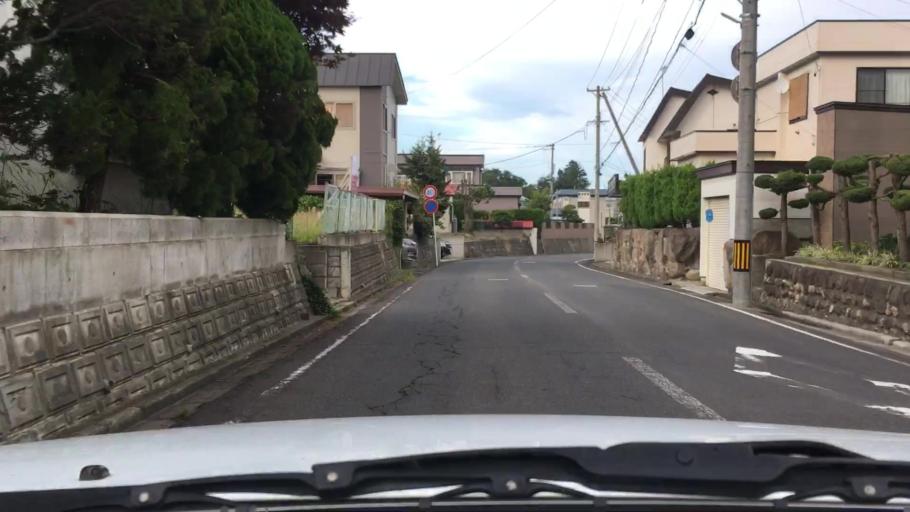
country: JP
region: Aomori
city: Hirosaki
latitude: 40.5752
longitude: 140.4538
